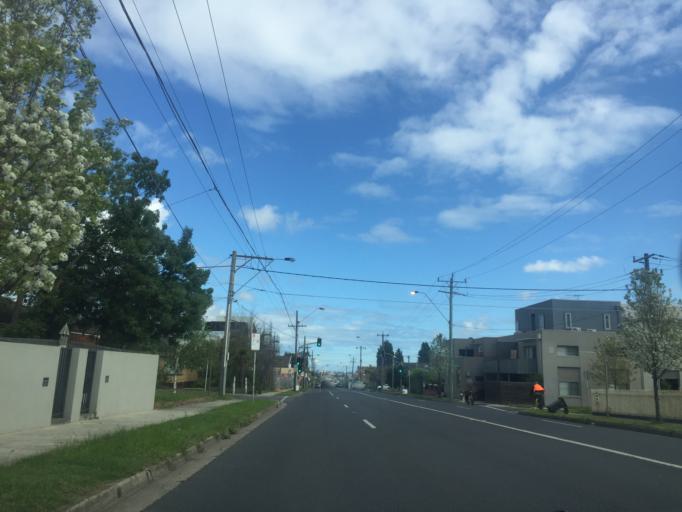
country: AU
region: Victoria
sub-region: Darebin
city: Reservoir
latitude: -37.7257
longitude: 145.0063
